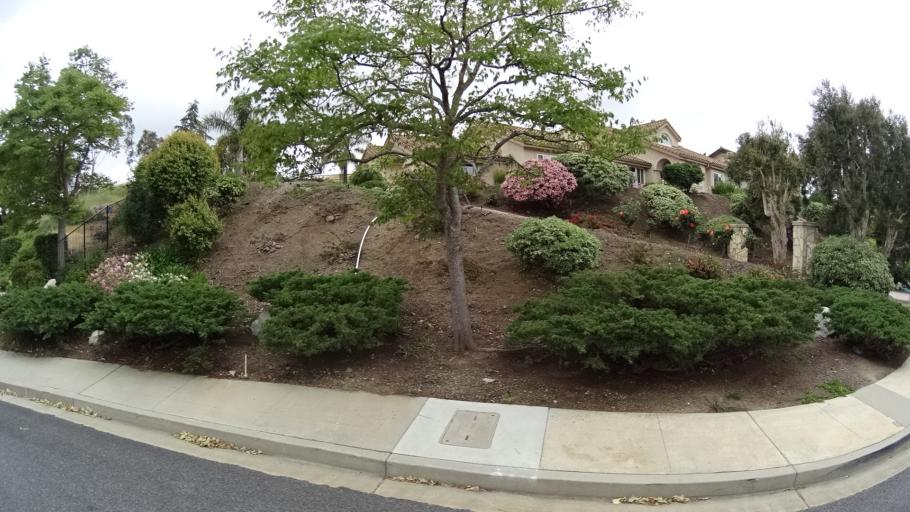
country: US
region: California
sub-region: Ventura County
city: Moorpark
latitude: 34.2289
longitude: -118.8889
